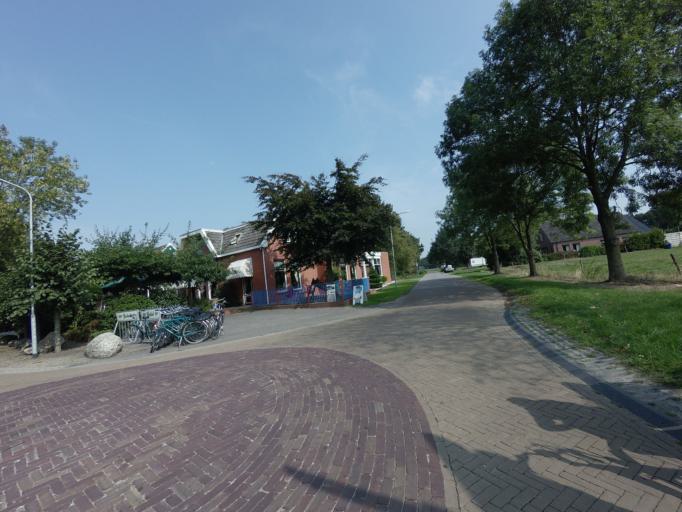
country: NL
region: Drenthe
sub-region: Gemeente Assen
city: Assen
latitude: 52.9550
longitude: 6.6032
